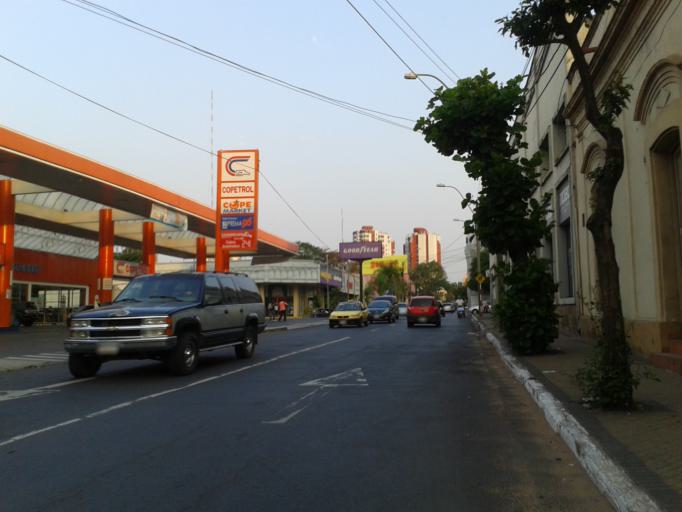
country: PY
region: Asuncion
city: Asuncion
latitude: -25.2830
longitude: -57.6307
